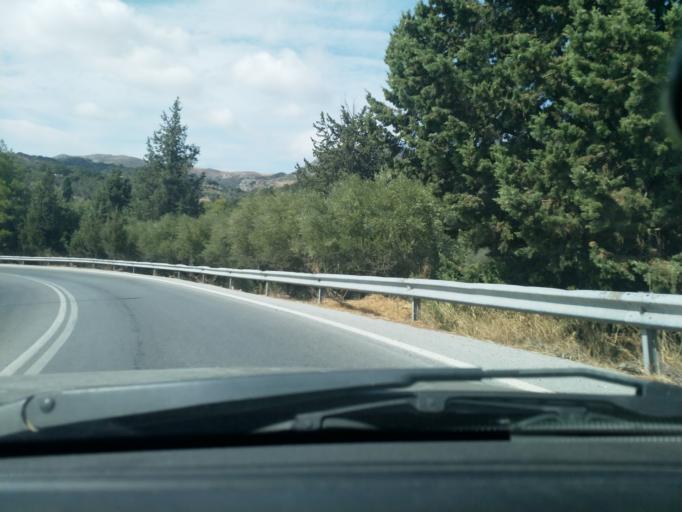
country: GR
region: Crete
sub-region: Nomos Rethymnis
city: Agia Foteini
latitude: 35.2205
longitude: 24.5272
